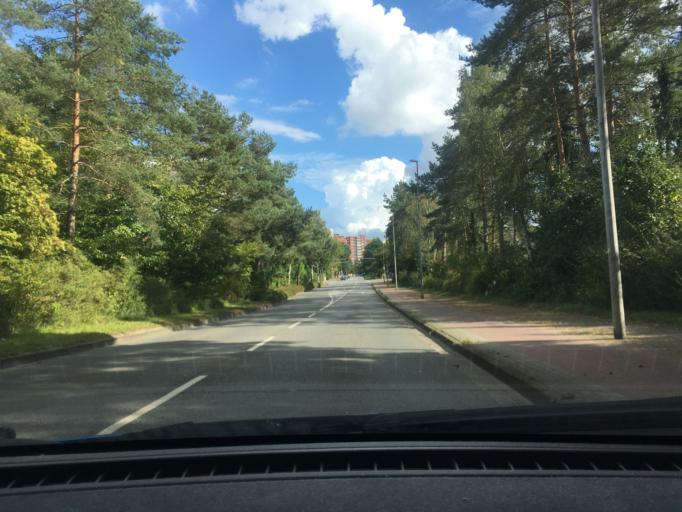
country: DE
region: Lower Saxony
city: Lueneburg
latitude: 53.2386
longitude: 10.4258
